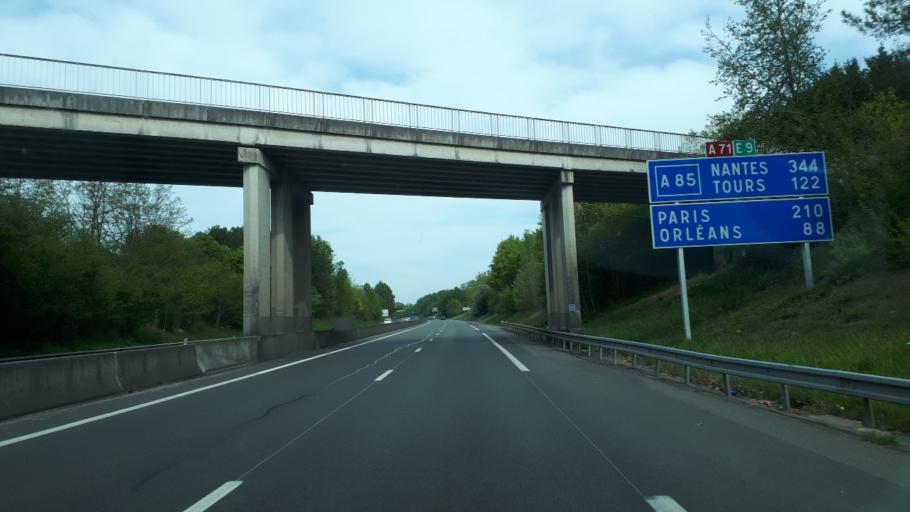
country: FR
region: Centre
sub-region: Departement du Cher
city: Vierzon
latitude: 47.2230
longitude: 2.1087
